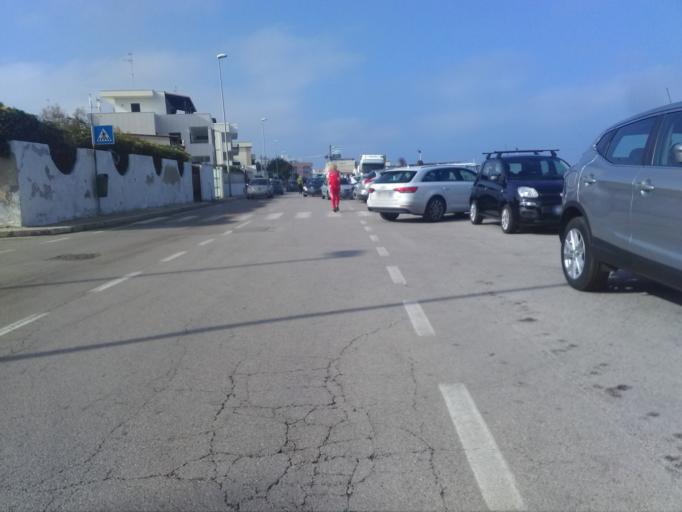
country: IT
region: Apulia
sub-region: Provincia di Bari
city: San Paolo
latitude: 41.1626
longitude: 16.7610
